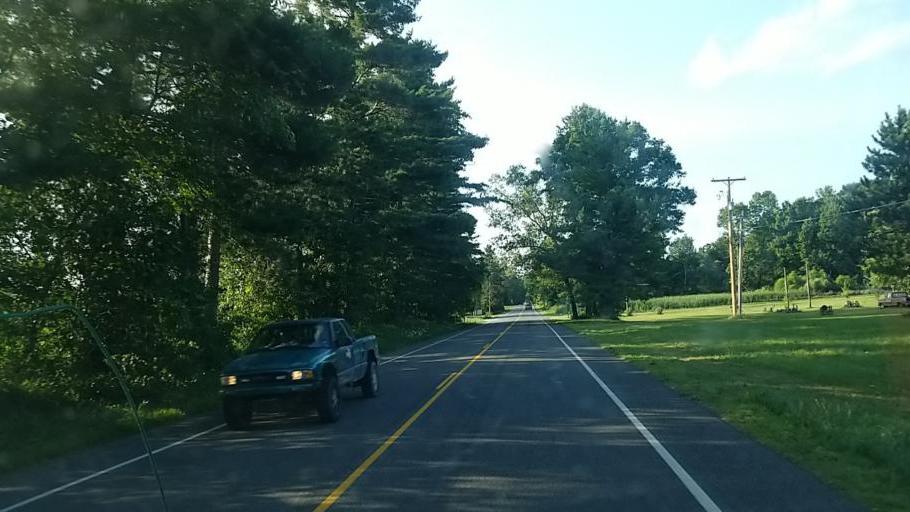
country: US
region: Michigan
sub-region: Montcalm County
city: Greenville
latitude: 43.2051
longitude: -85.3518
